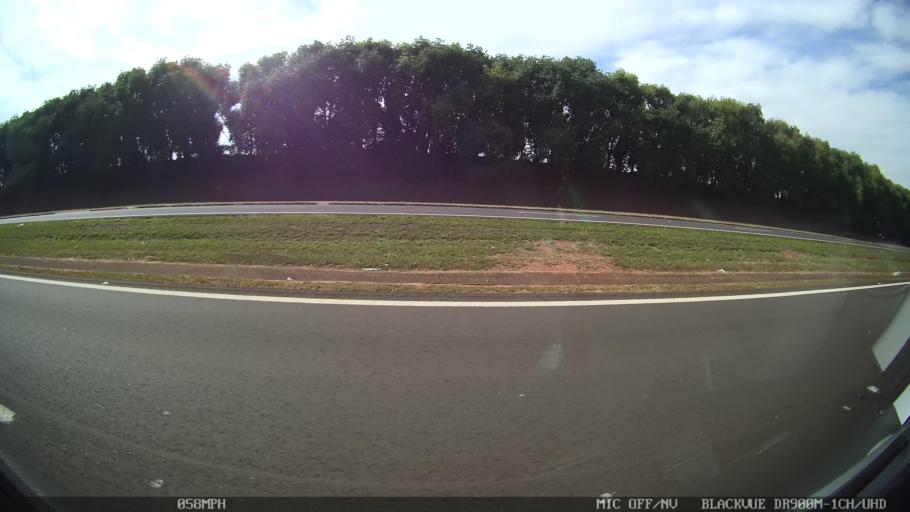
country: BR
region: Sao Paulo
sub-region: Matao
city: Matao
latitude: -21.6279
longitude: -48.4068
